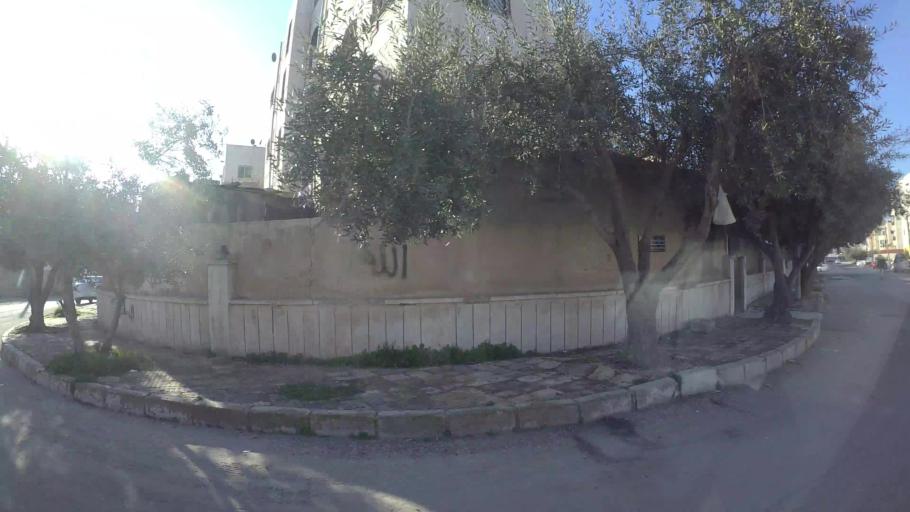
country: JO
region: Amman
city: Al Bunayyat ash Shamaliyah
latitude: 31.8966
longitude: 35.9124
